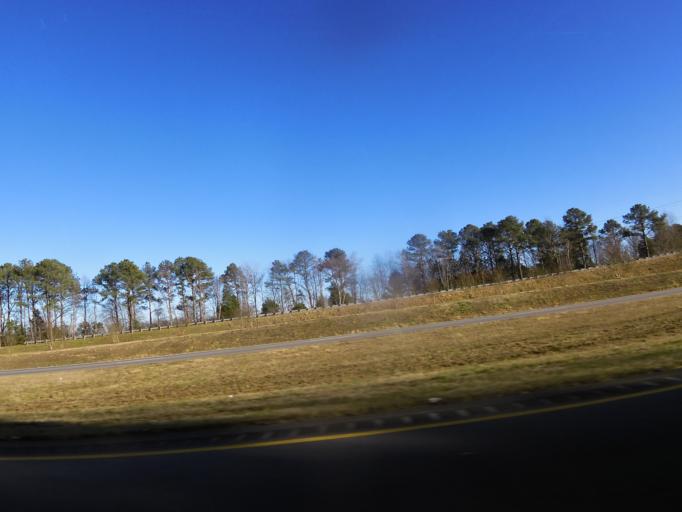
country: US
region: Virginia
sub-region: City of Suffolk
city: Suffolk
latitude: 36.7466
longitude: -76.6136
